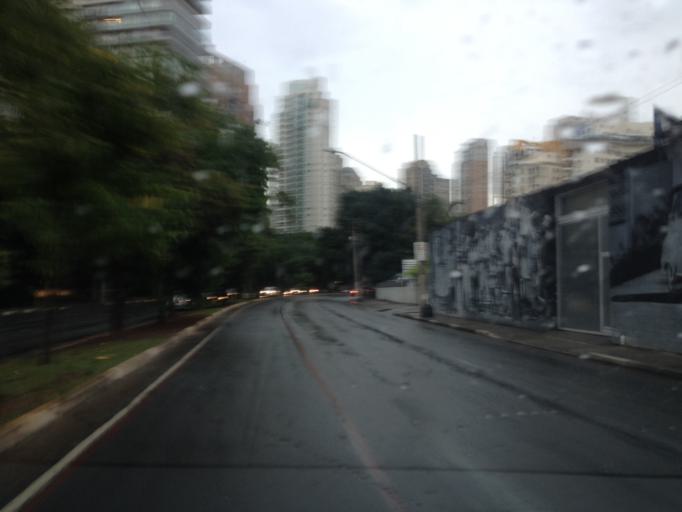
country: BR
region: Sao Paulo
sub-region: Sao Paulo
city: Sao Paulo
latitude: -23.5980
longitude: -46.6700
